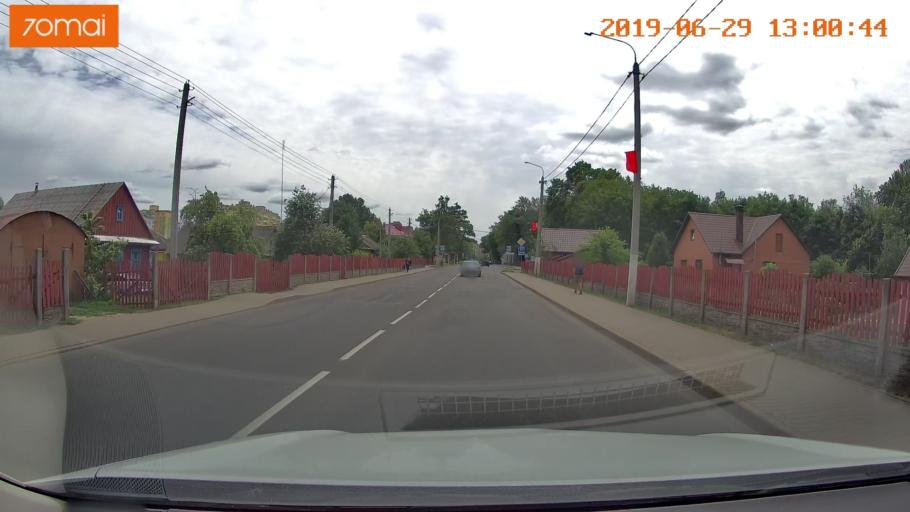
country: BY
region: Minsk
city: Slutsk
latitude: 53.0429
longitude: 27.5579
